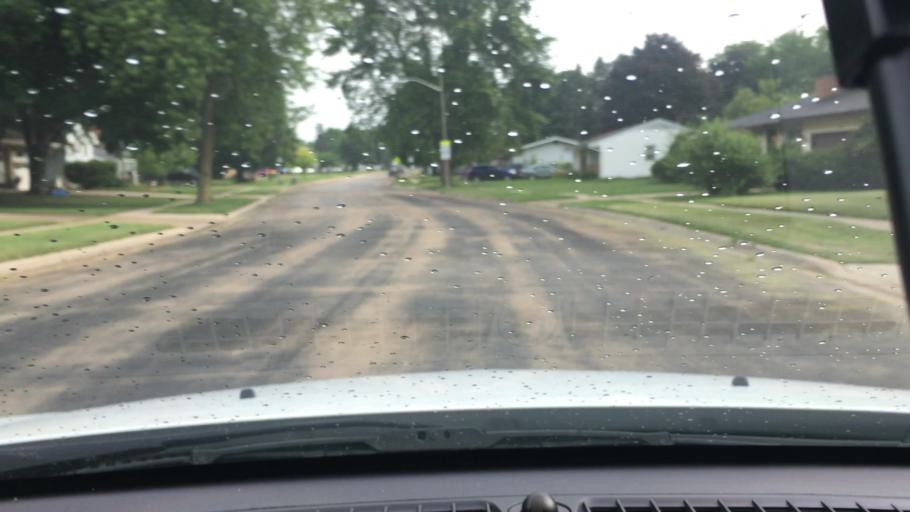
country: US
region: Illinois
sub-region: Ogle County
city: Rochelle
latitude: 41.9316
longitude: -89.0632
